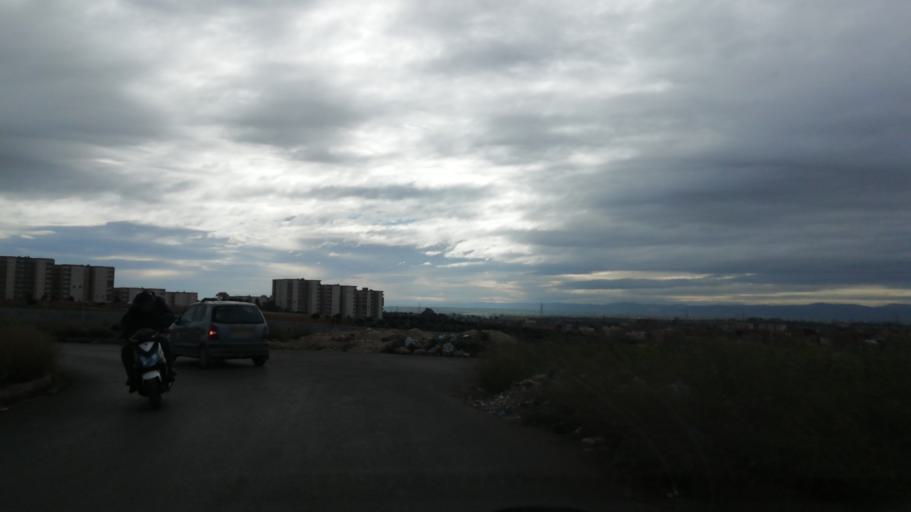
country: DZ
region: Oran
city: Oran
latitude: 35.6921
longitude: -0.5980
